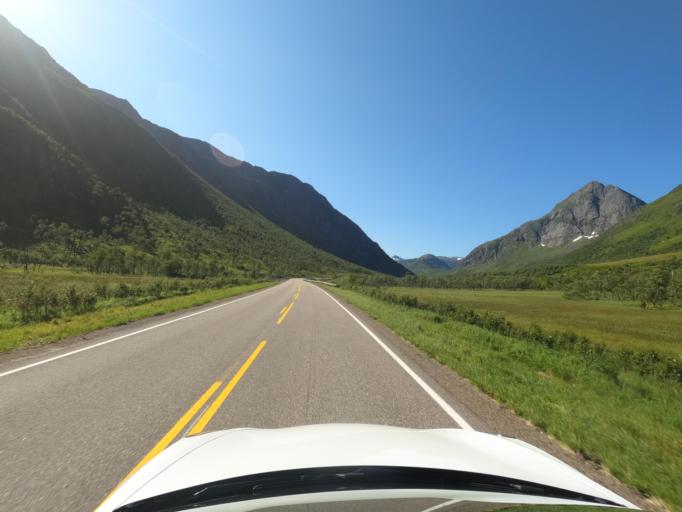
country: NO
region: Nordland
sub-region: Lodingen
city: Lodingen
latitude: 68.5132
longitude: 15.7363
